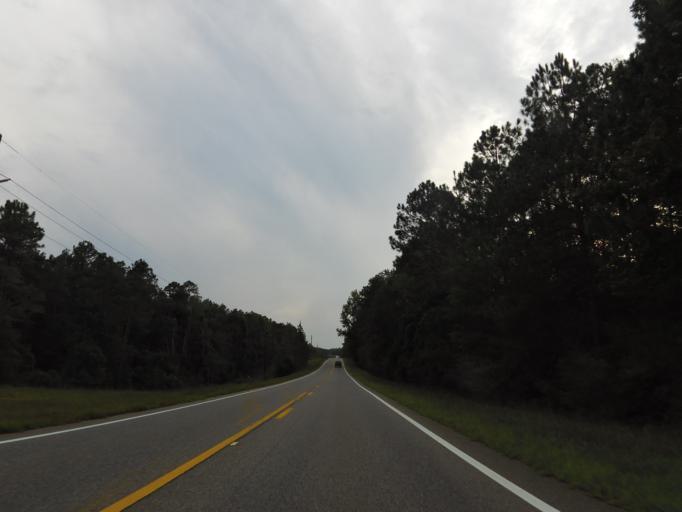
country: US
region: Alabama
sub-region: Baldwin County
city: Bay Minette
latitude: 30.9139
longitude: -87.7151
